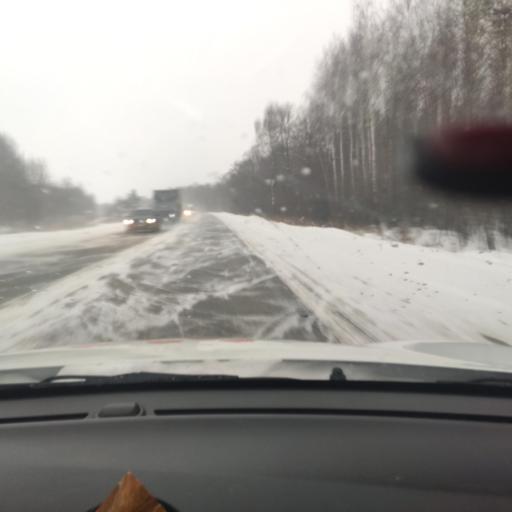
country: RU
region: Tatarstan
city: Verkhniy Uslon
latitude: 55.6902
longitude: 48.8751
